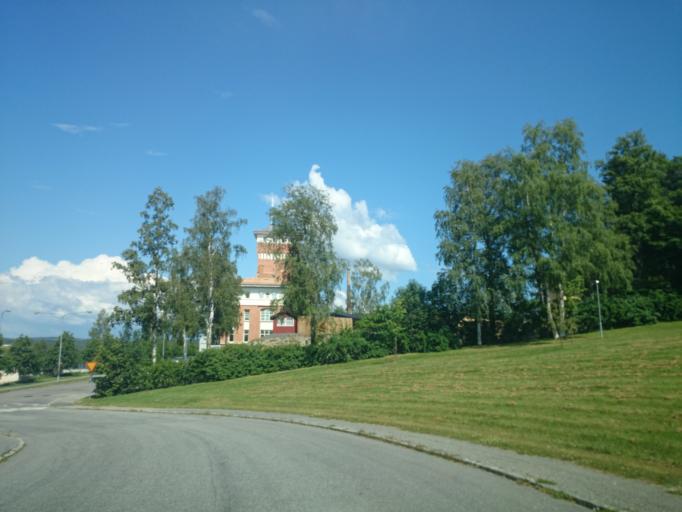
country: SE
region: Vaesternorrland
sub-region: Haernoesands Kommun
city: Haernoesand
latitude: 62.6389
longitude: 17.9508
